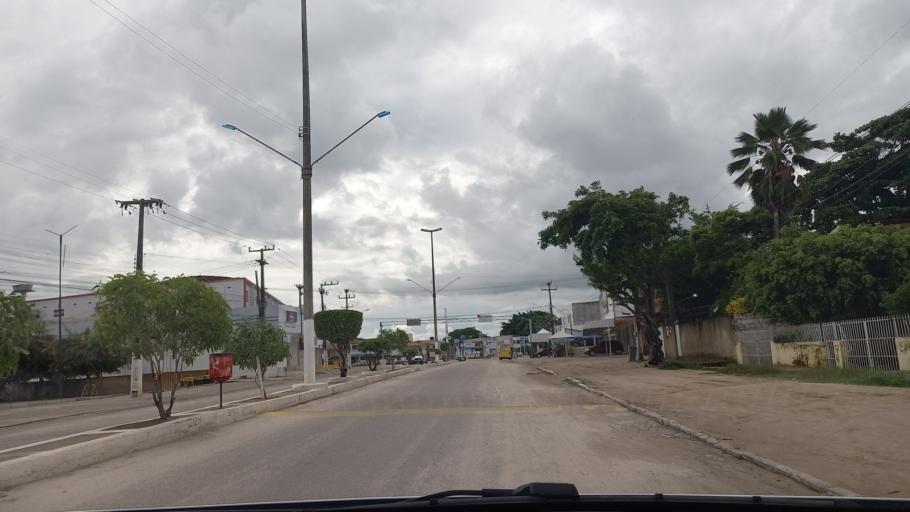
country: BR
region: Pernambuco
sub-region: Sao Jose Da Coroa Grande
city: Sao Jose da Coroa Grande
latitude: -8.8953
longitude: -35.1492
